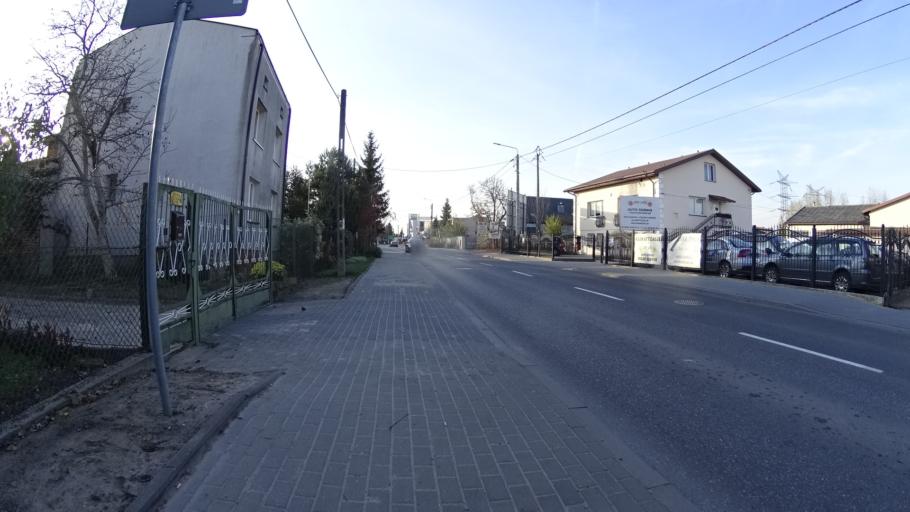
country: PL
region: Masovian Voivodeship
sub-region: Powiat warszawski zachodni
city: Babice
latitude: 52.2878
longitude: 20.8730
